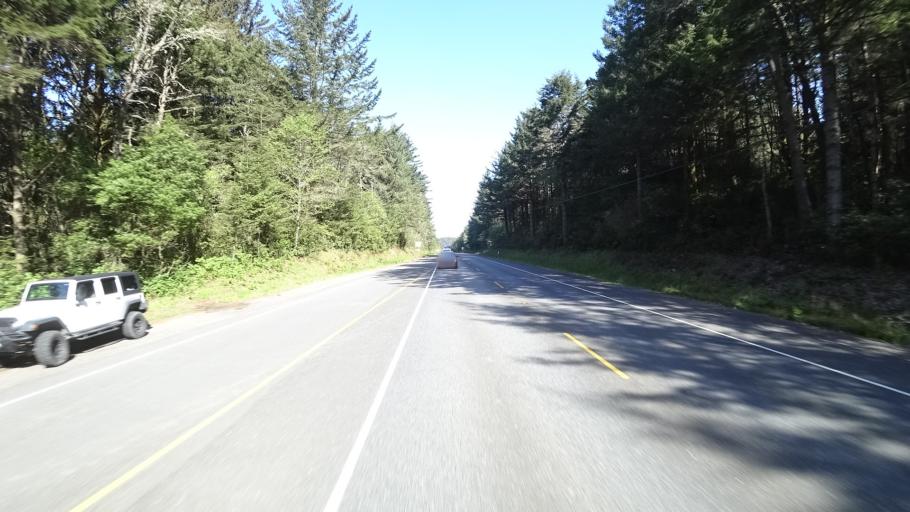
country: US
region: Oregon
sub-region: Curry County
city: Brookings
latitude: 42.0937
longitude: -124.3348
